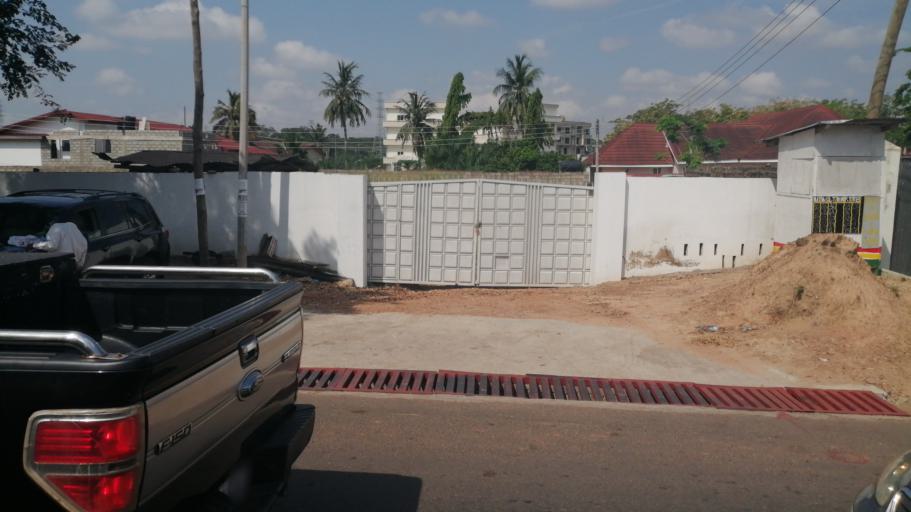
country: GH
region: Greater Accra
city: Medina Estates
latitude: 5.6359
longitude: -0.1720
